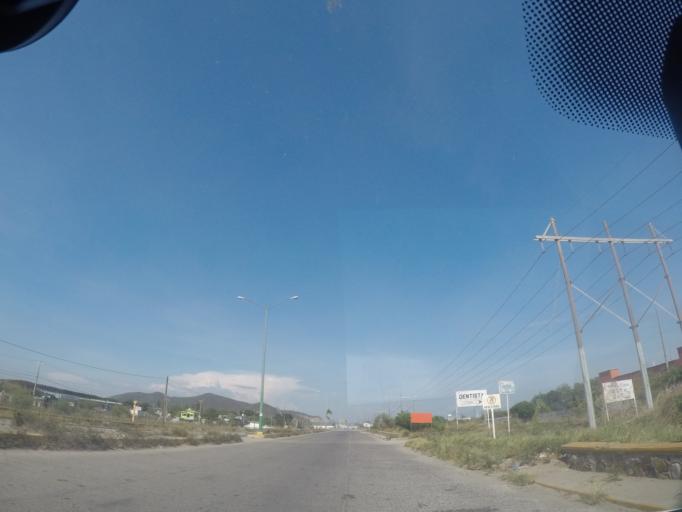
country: MX
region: Oaxaca
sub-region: Salina Cruz
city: Salina Cruz
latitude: 16.2199
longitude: -95.1929
